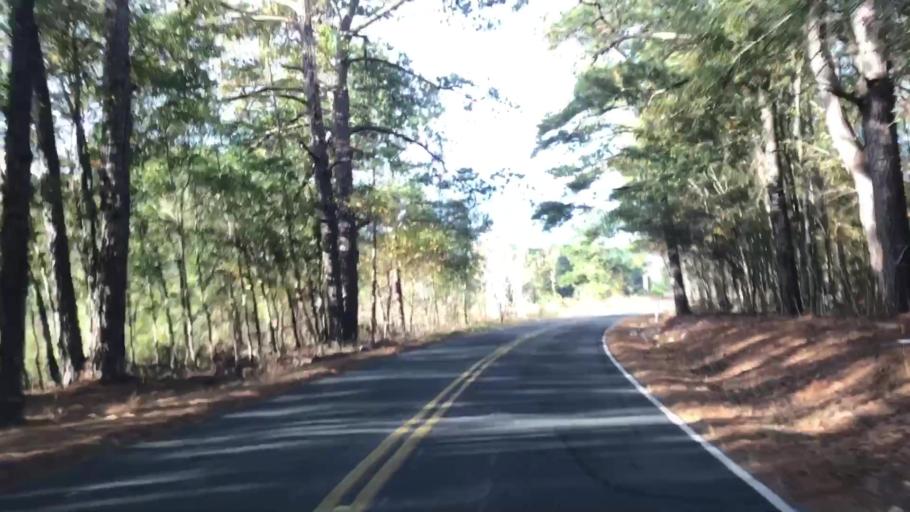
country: US
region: South Carolina
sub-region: Charleston County
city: Ravenel
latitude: 32.7668
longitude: -80.2223
